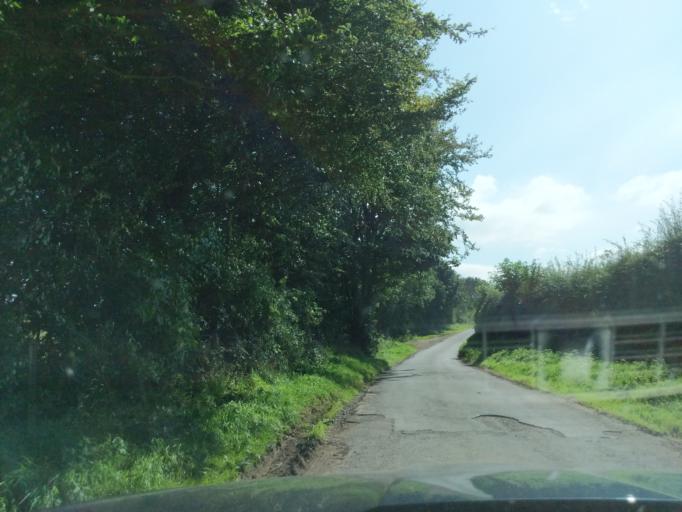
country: GB
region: England
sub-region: Northumberland
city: Ford
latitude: 55.6399
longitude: -2.1371
